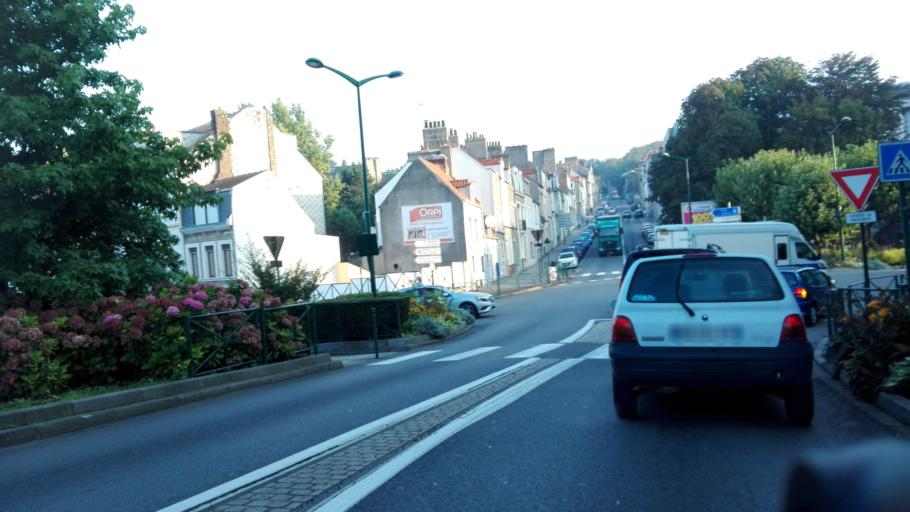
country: FR
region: Nord-Pas-de-Calais
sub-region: Departement du Pas-de-Calais
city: Boulogne-sur-Mer
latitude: 50.7195
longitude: 1.6151
